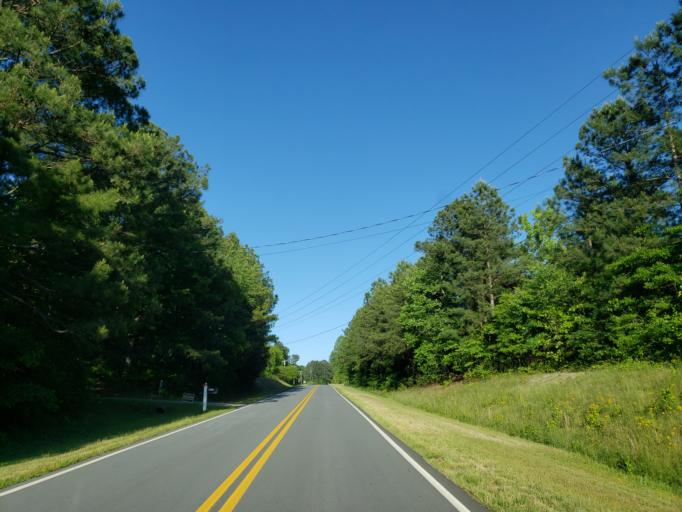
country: US
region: Georgia
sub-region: Haralson County
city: Buchanan
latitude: 33.8103
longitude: -85.2270
